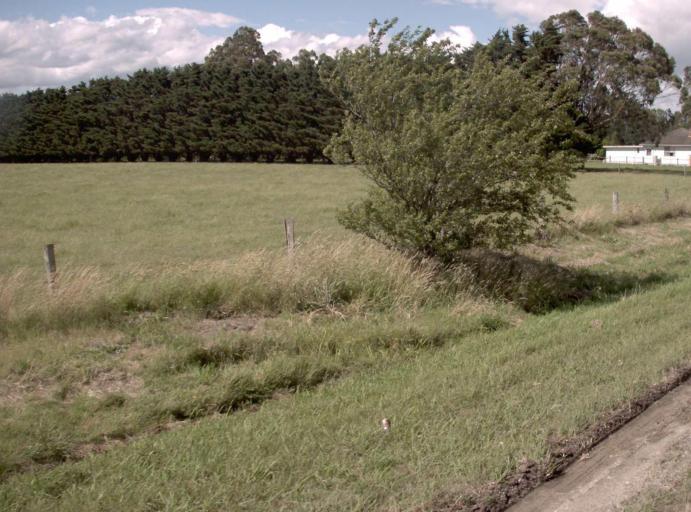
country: AU
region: Victoria
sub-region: Latrobe
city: Traralgon
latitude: -38.1313
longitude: 146.5567
